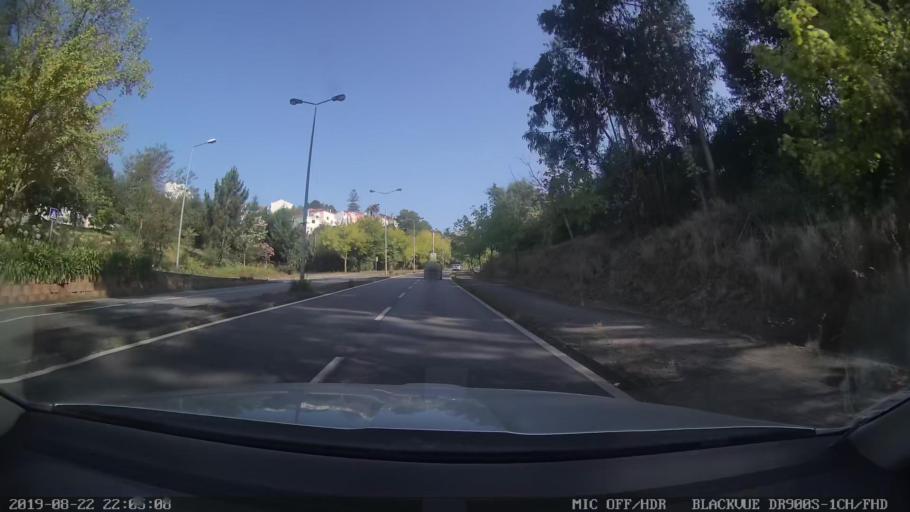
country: PT
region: Coimbra
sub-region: Coimbra
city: Coimbra
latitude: 40.2137
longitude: -8.4035
